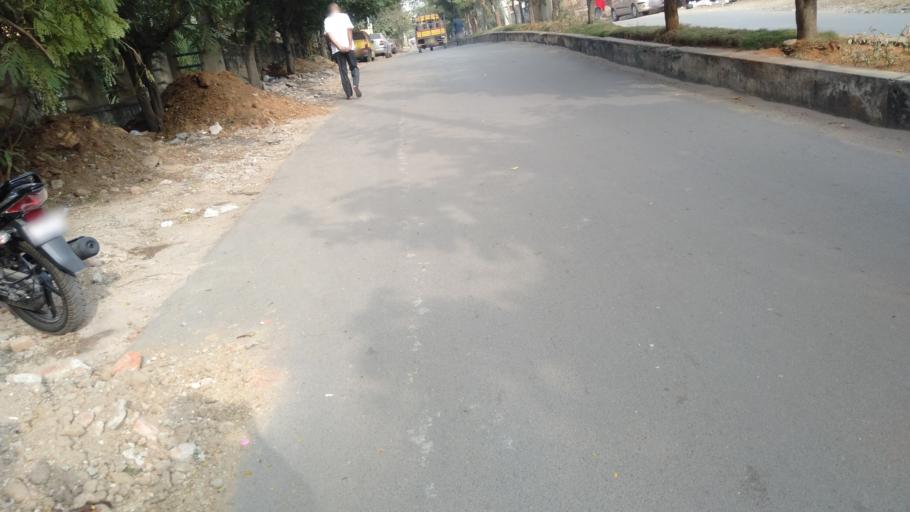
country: IN
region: Telangana
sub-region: Rangareddi
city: Kukatpalli
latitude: 17.4896
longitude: 78.3864
